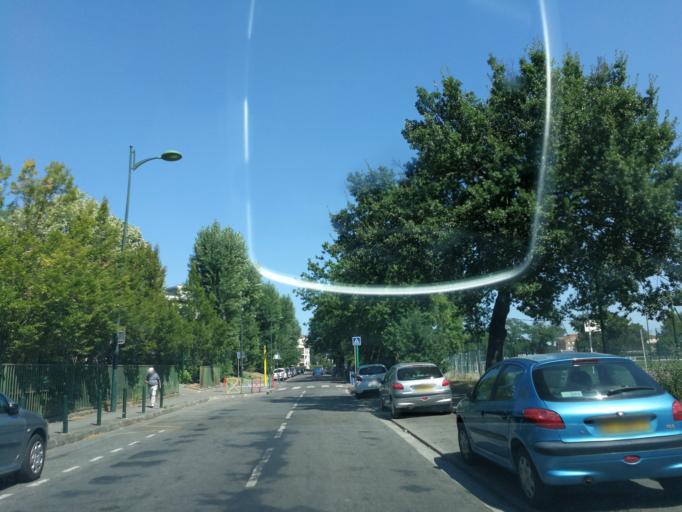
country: FR
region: Midi-Pyrenees
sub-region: Departement de la Haute-Garonne
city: Toulouse
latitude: 43.6266
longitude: 1.4683
